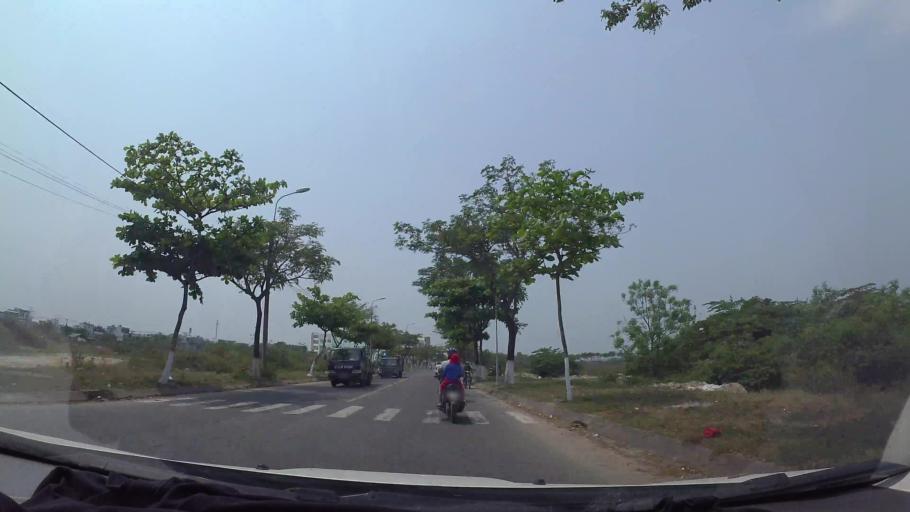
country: VN
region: Da Nang
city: Cam Le
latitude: 16.0068
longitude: 108.2111
